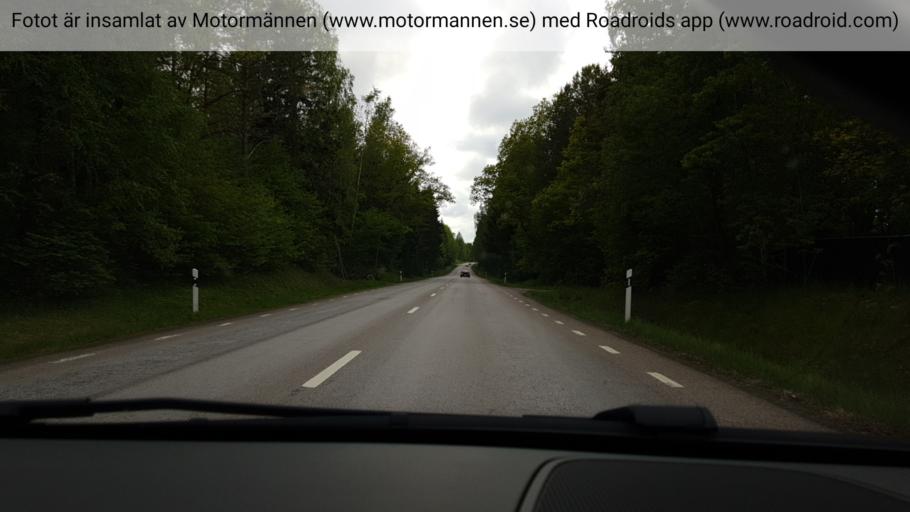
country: SE
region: Uppsala
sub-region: Osthammars Kommun
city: Osterbybruk
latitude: 60.1947
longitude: 17.8654
